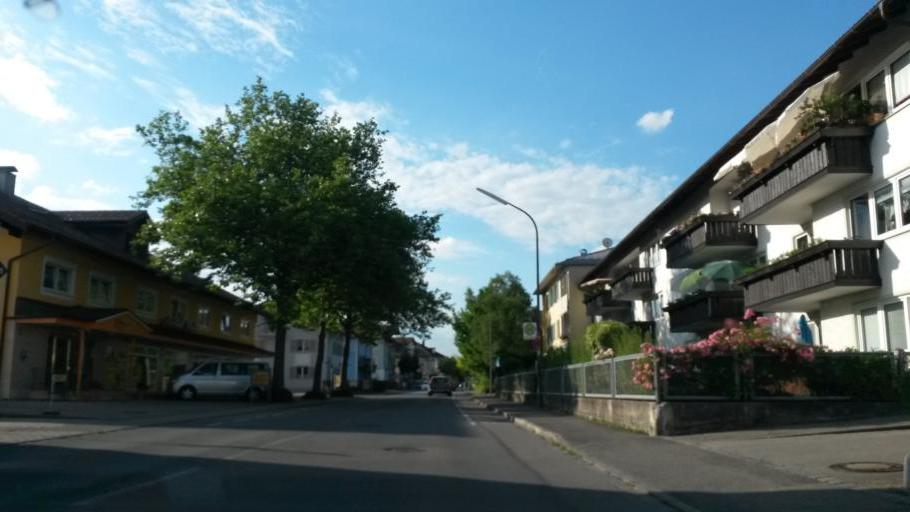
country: DE
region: Bavaria
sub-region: Upper Bavaria
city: Prien am Chiemsee
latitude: 47.8501
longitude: 12.3484
